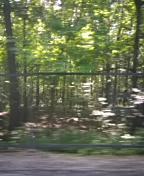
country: RU
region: Moscow
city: Pokrovskoye-Streshnevo
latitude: 55.8217
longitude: 37.4656
